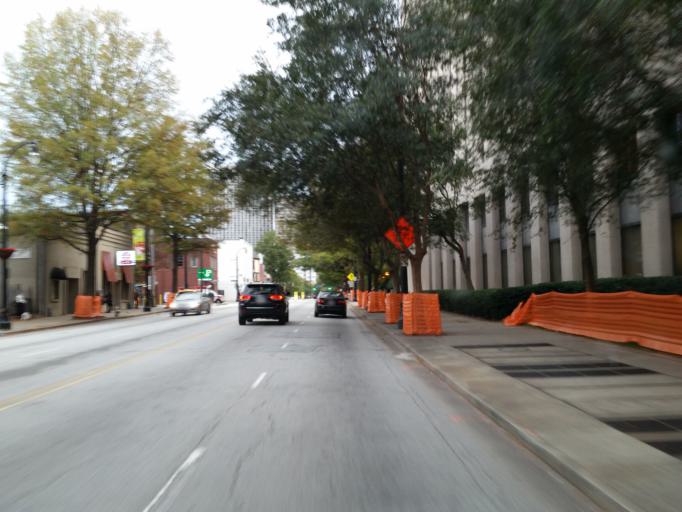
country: US
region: Georgia
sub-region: Fulton County
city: Atlanta
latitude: 33.7696
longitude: -84.3852
